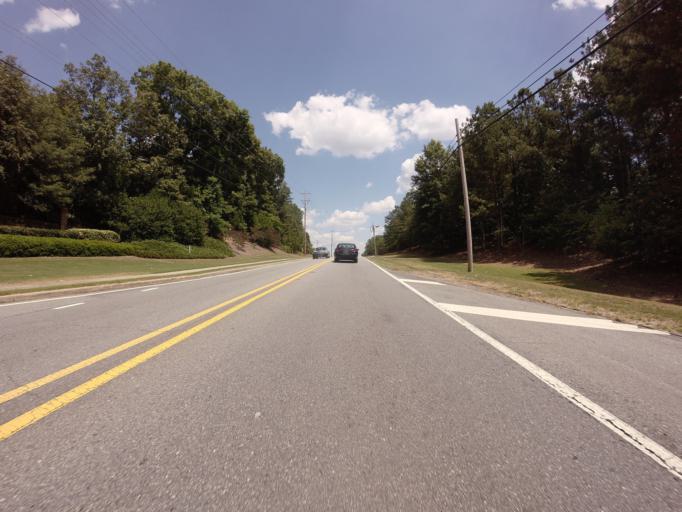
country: US
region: Georgia
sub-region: Fulton County
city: Johns Creek
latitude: 34.0190
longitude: -84.2427
